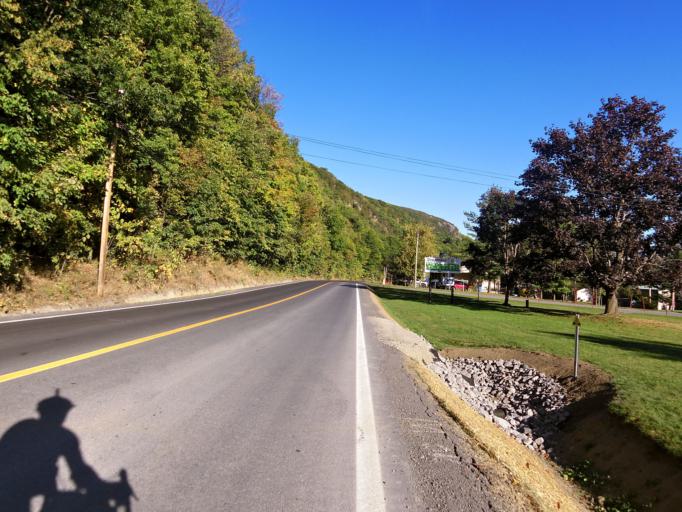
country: CA
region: Ontario
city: Bells Corners
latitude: 45.4900
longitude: -75.8840
